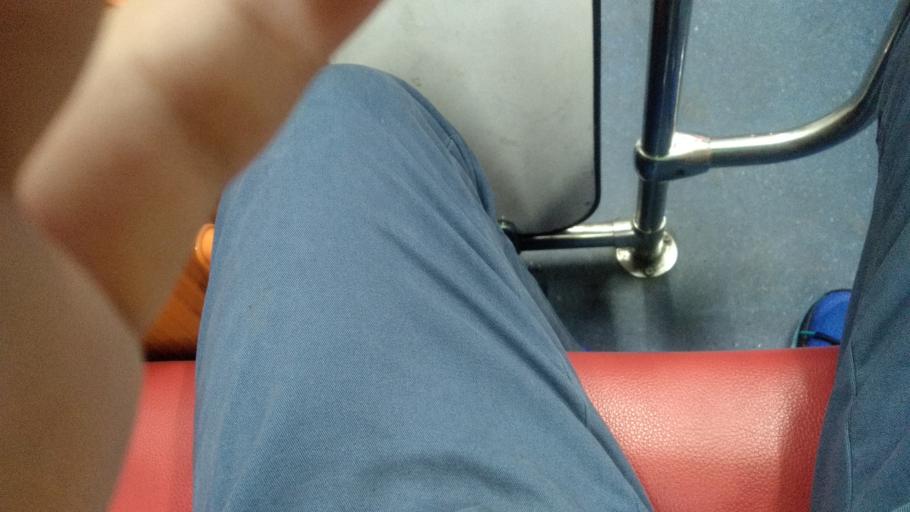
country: TW
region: Taiwan
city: Taoyuan City
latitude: 24.9894
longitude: 121.1789
